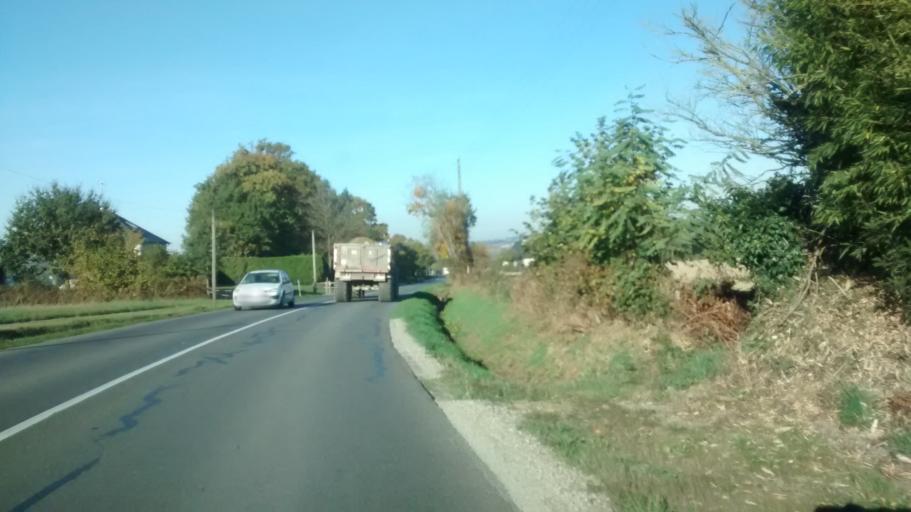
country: FR
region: Brittany
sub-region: Departement d'Ille-et-Vilaine
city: Montreuil-sous-Perouse
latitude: 48.1357
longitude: -1.2349
